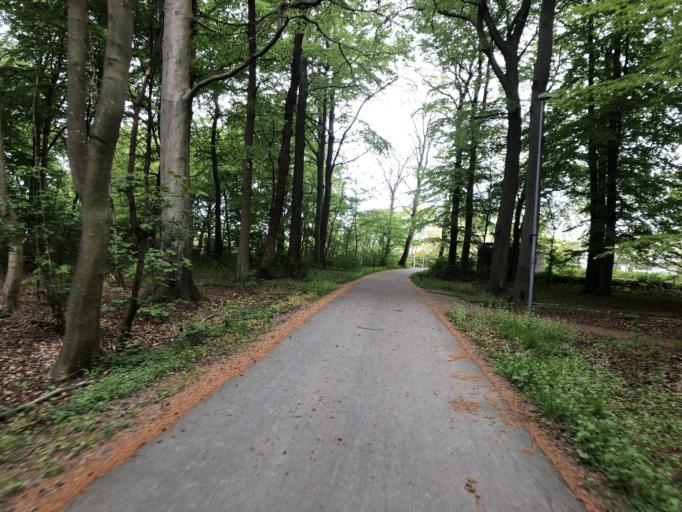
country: SE
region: Skane
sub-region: Landskrona
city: Landskrona
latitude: 55.8933
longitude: 12.8331
